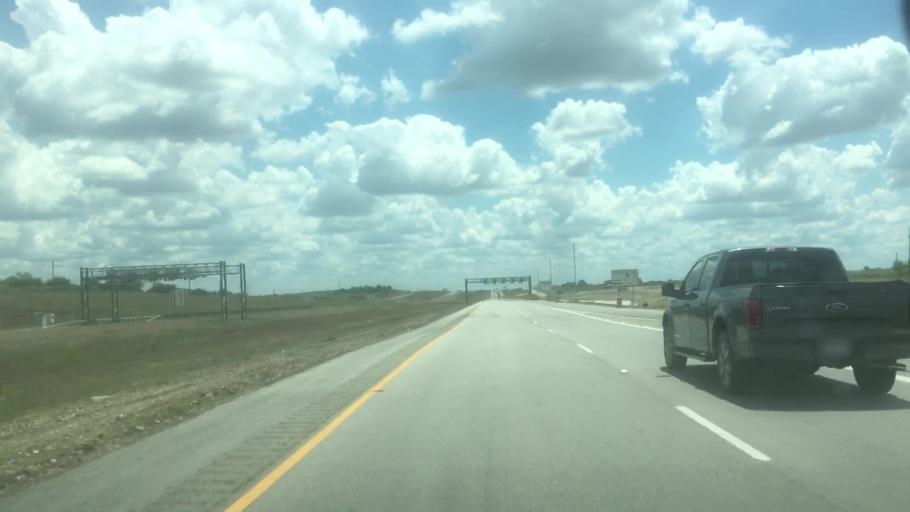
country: US
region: Texas
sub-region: Caldwell County
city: Uhland
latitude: 29.9925
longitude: -97.6849
